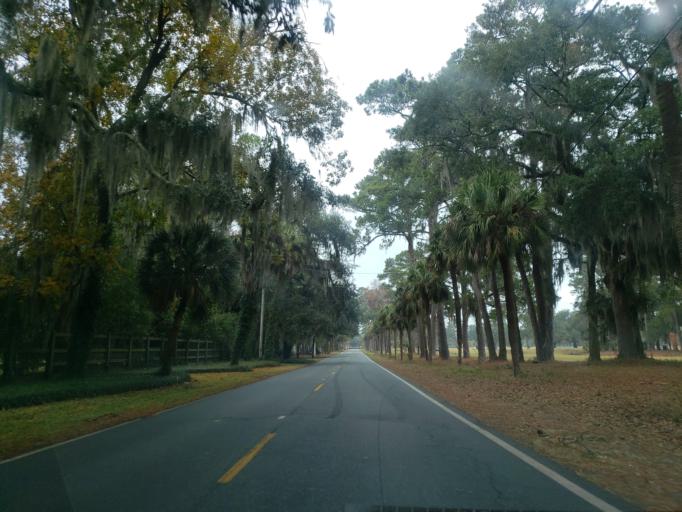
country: US
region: Georgia
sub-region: Chatham County
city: Wilmington Island
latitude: 31.9997
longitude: -80.9966
